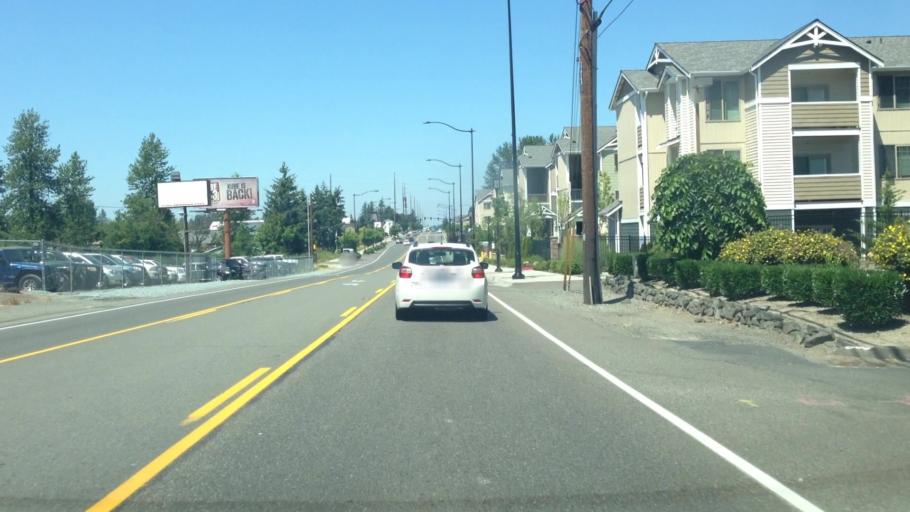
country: US
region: Washington
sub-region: Pierce County
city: Edgewood
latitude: 47.2317
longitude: -122.2939
